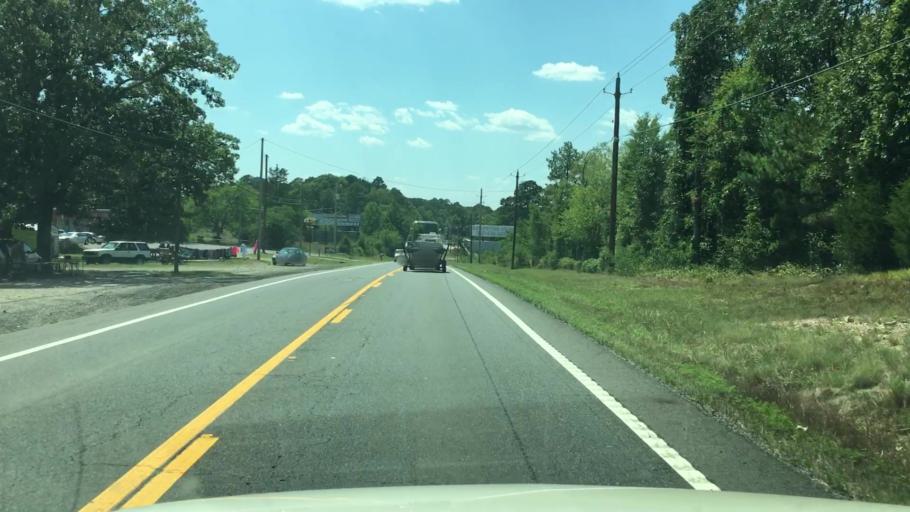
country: US
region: Arkansas
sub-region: Garland County
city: Piney
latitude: 34.5095
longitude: -93.1595
